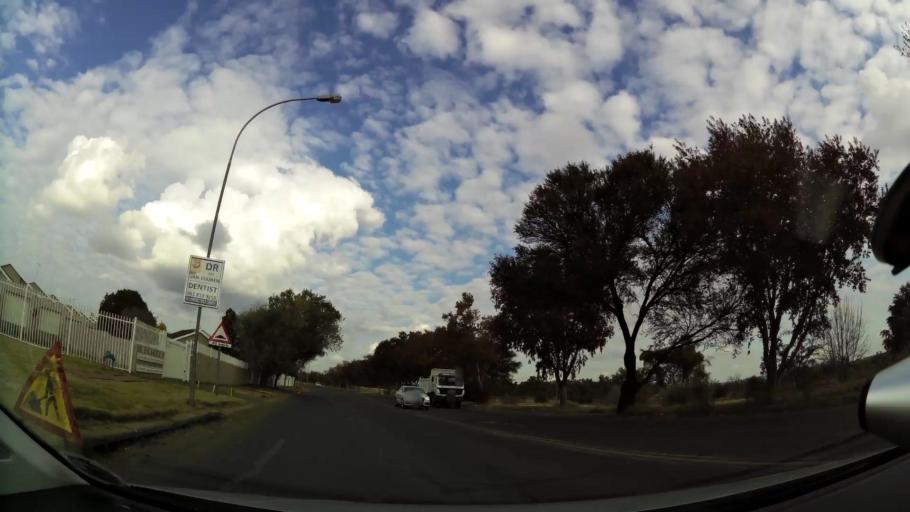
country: ZA
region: Orange Free State
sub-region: Mangaung Metropolitan Municipality
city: Bloemfontein
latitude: -29.0772
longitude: 26.1933
